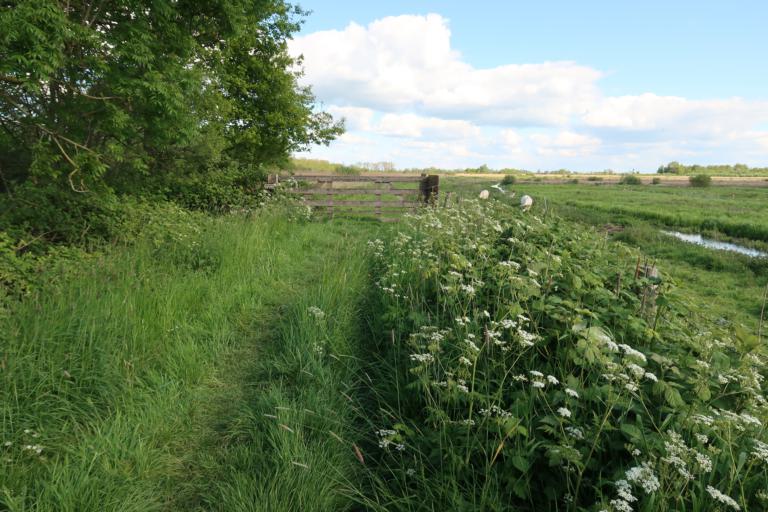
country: NL
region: Utrecht
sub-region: Gemeente Lopik
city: Lopik
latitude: 51.9580
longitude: 4.9855
